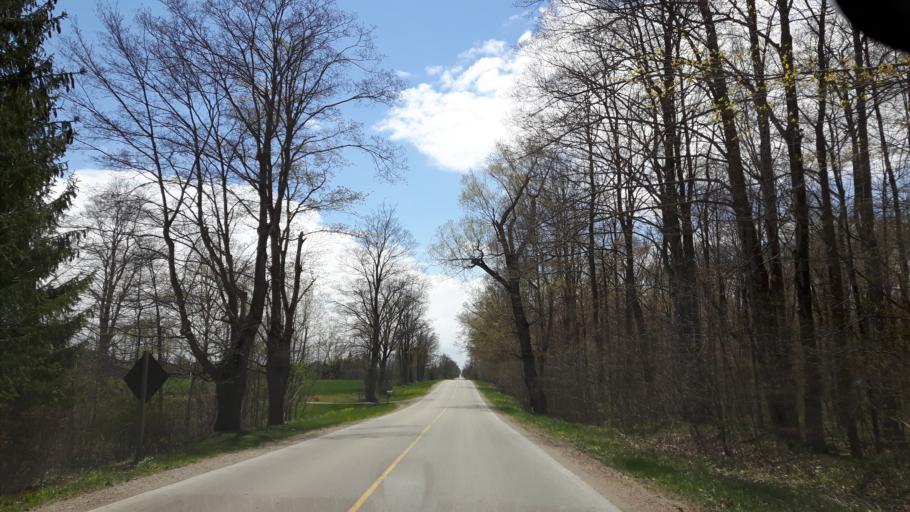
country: CA
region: Ontario
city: Bluewater
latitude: 43.5410
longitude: -81.6748
